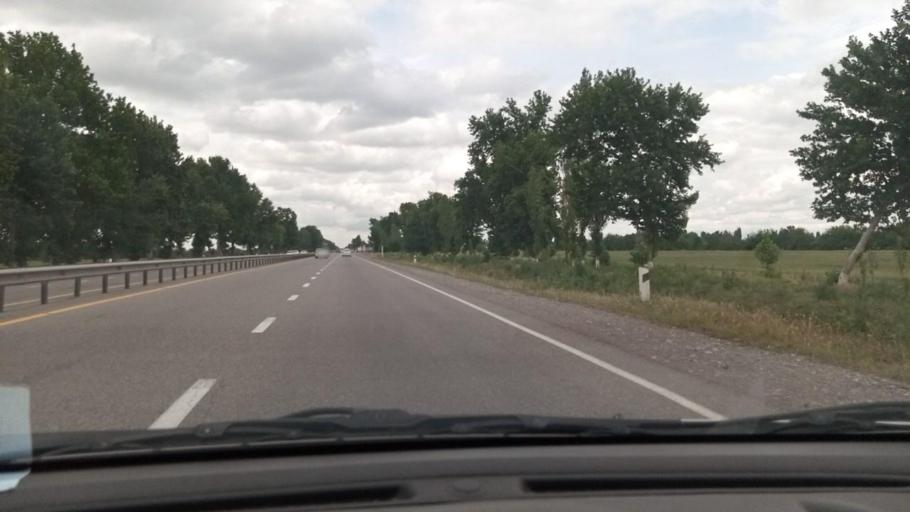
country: UZ
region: Toshkent Shahri
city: Bektemir
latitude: 41.2024
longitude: 69.4030
